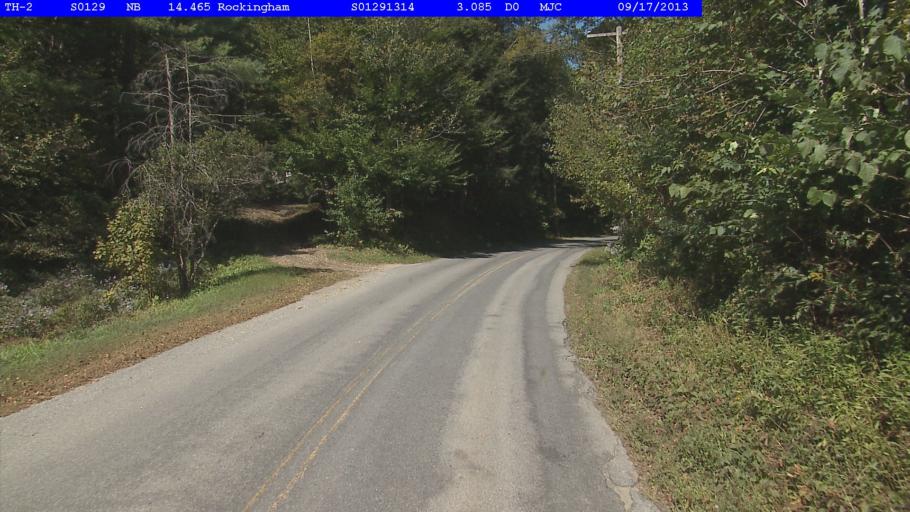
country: US
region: Vermont
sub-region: Windham County
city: Rockingham
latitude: 43.1618
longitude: -72.5176
